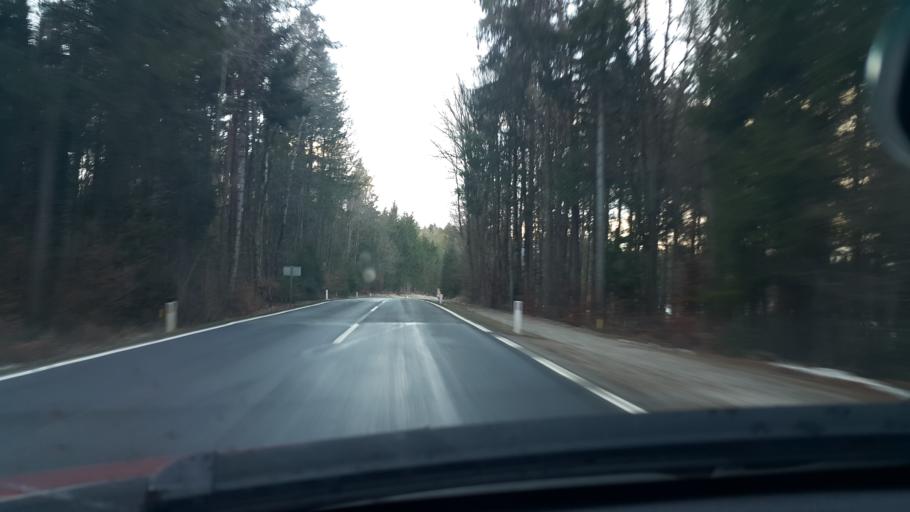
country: AT
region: Styria
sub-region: Politischer Bezirk Deutschlandsberg
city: Sankt Peter im Sulmtal
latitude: 46.7777
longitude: 15.2503
